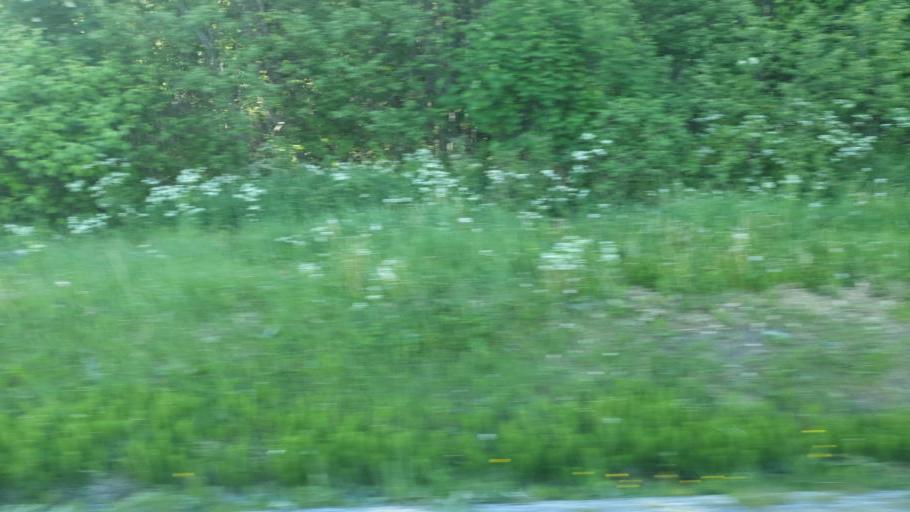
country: NO
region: Sor-Trondelag
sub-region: Skaun
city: Borsa
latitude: 63.5032
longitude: 10.1280
